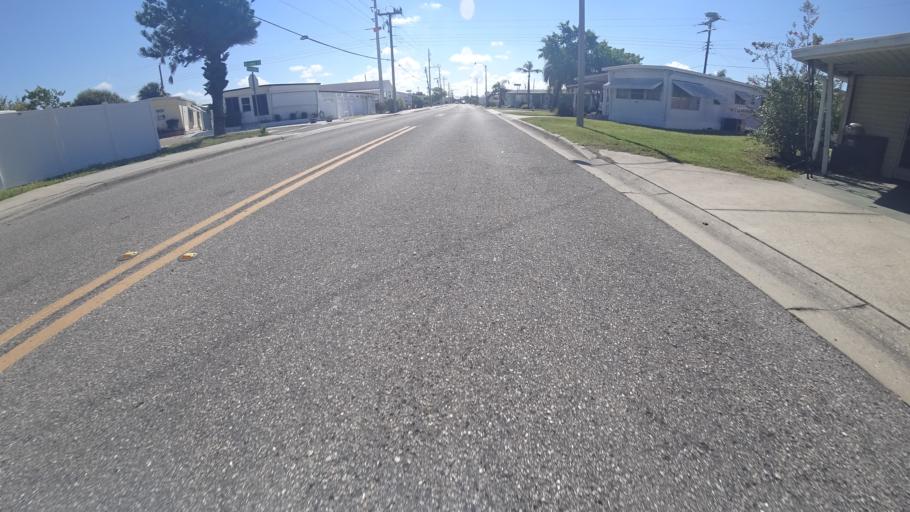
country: US
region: Florida
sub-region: Manatee County
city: Bayshore Gardens
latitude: 27.4228
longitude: -82.5841
